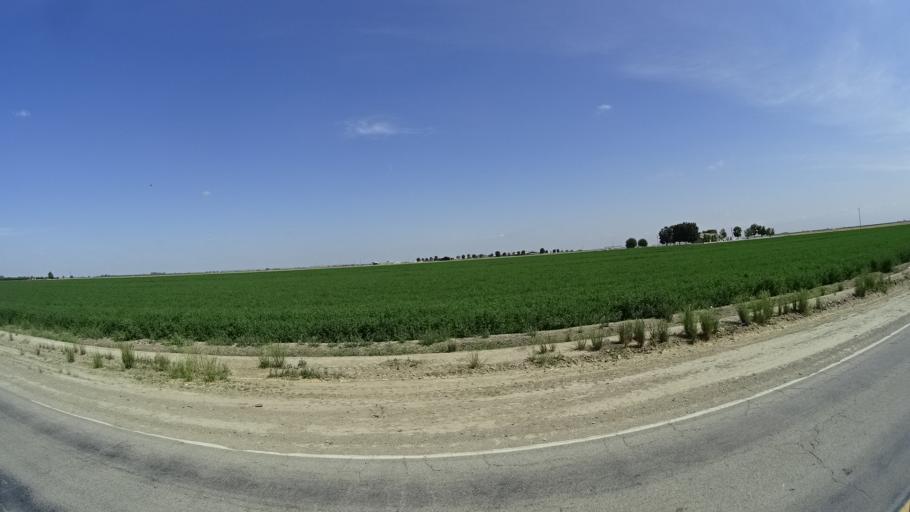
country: US
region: California
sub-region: Kings County
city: Home Garden
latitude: 36.2698
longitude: -119.5319
